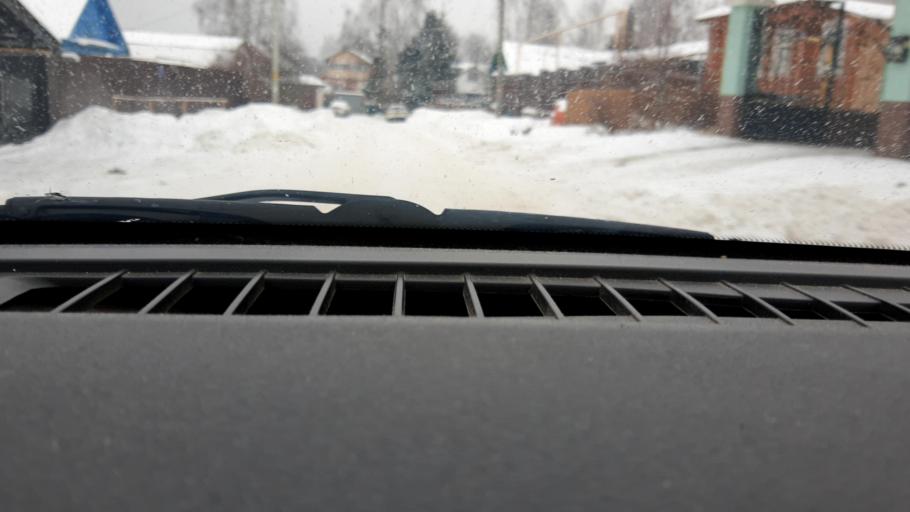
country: RU
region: Nizjnij Novgorod
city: Afonino
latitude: 56.1940
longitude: 44.0623
